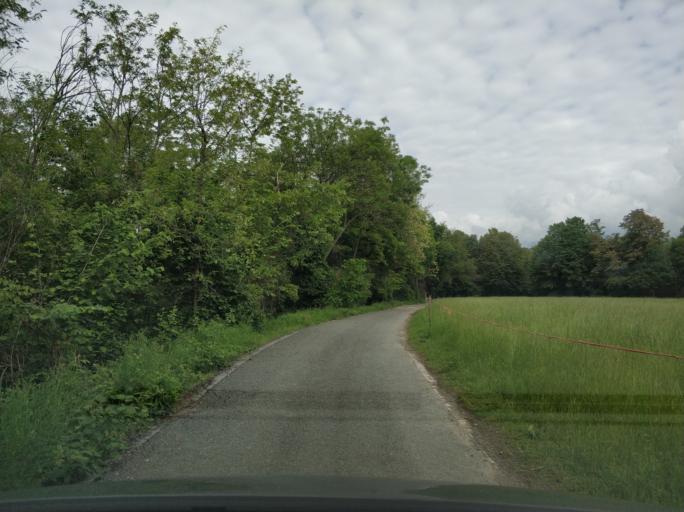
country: IT
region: Piedmont
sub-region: Provincia di Torino
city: Balangero
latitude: 45.2644
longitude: 7.5047
